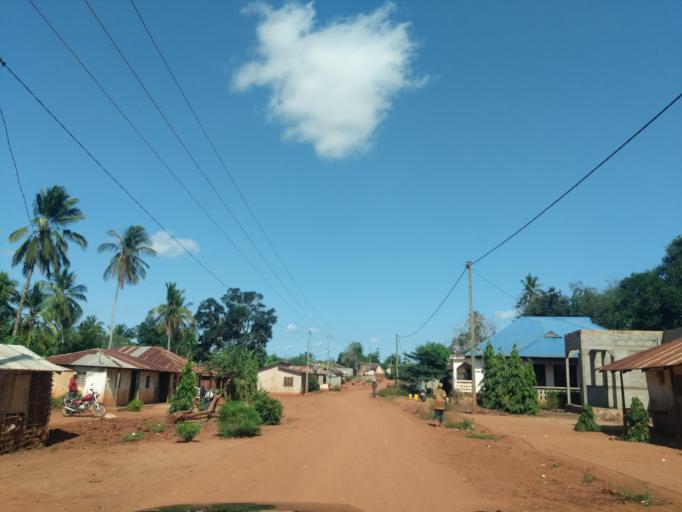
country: TZ
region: Tanga
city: Muheza
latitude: -5.3859
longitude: 38.5779
